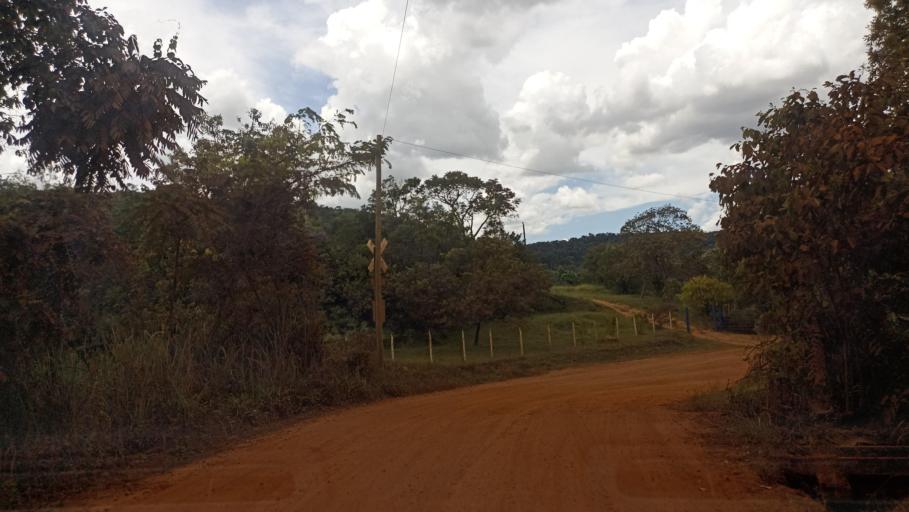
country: BR
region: Minas Gerais
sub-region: Itabirito
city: Itabirito
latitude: -20.3628
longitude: -43.7636
